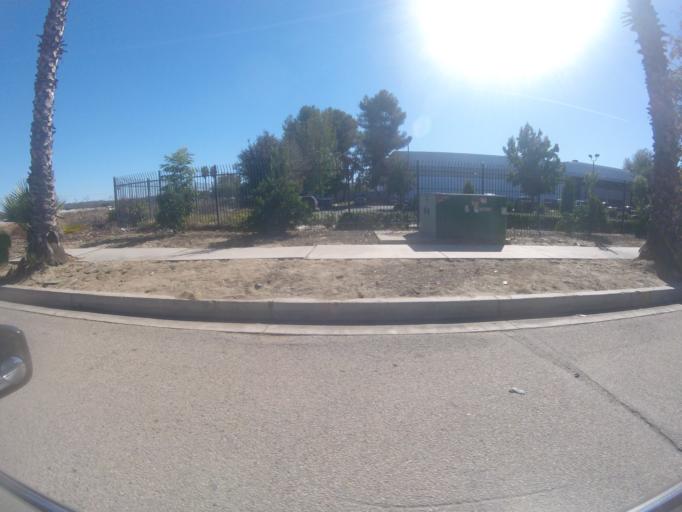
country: US
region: California
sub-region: San Bernardino County
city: Redlands
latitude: 34.0593
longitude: -117.2139
